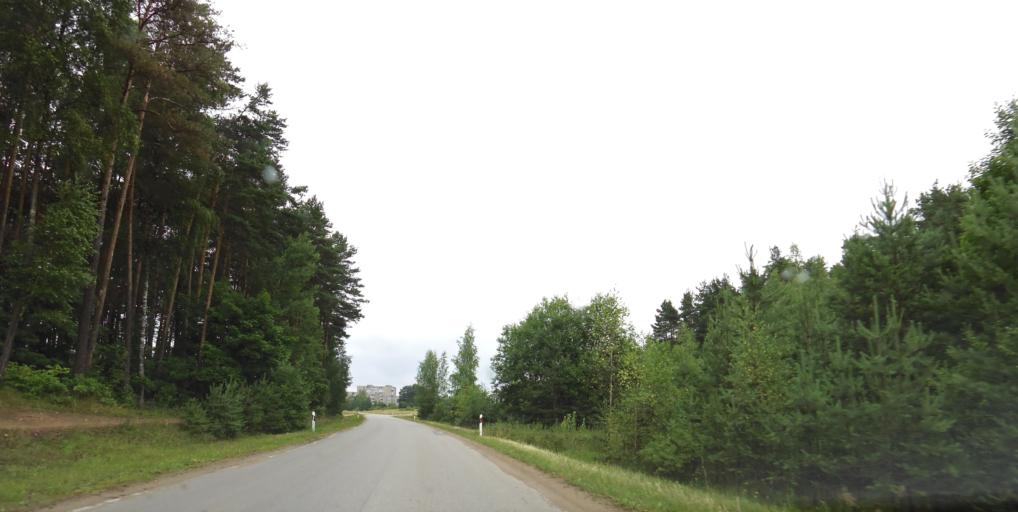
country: LT
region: Vilnius County
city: Pilaite
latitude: 54.6993
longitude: 25.1821
